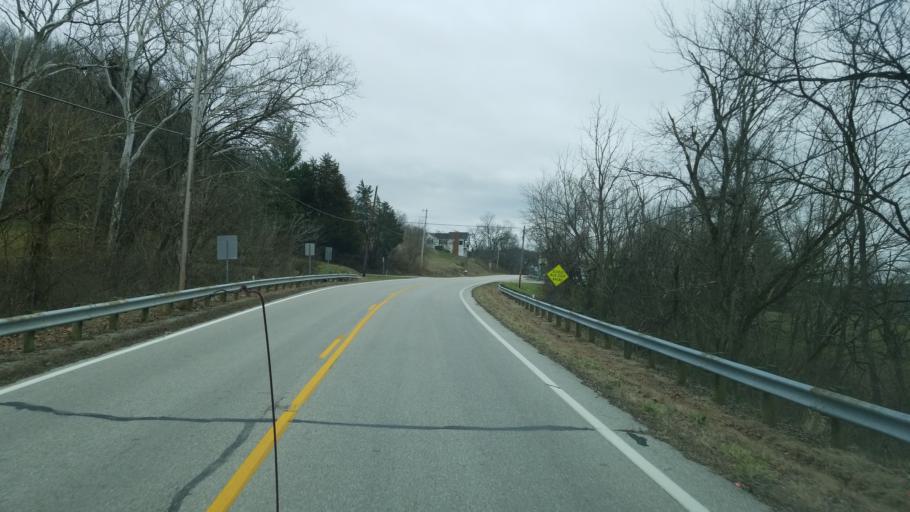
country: US
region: Ohio
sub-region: Brown County
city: Ripley
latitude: 38.7547
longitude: -83.8532
